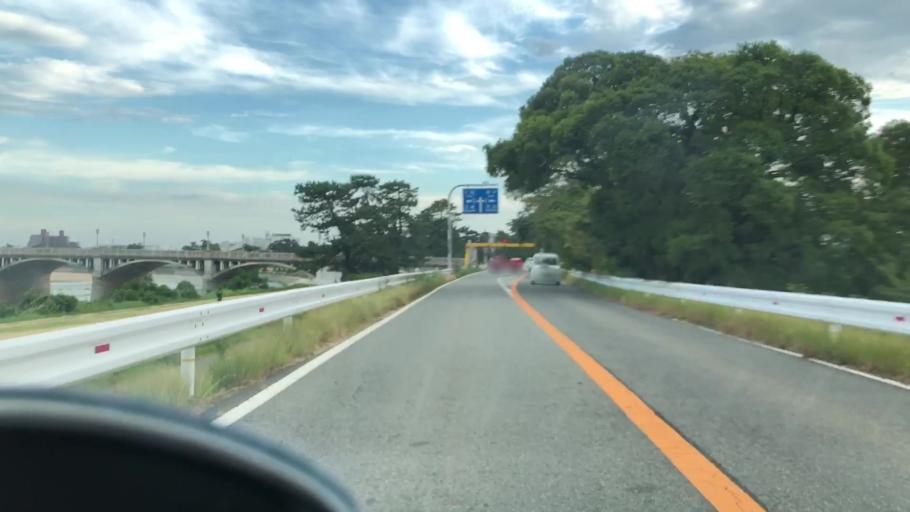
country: JP
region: Hyogo
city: Amagasaki
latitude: 34.7336
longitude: 135.3791
